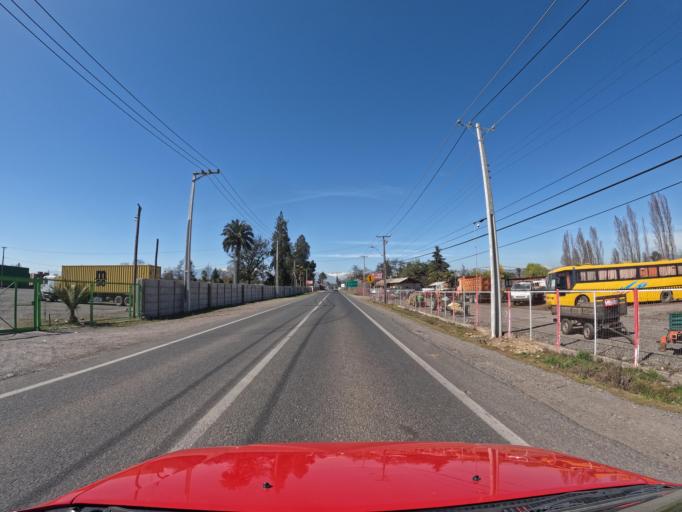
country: CL
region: Maule
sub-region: Provincia de Curico
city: Teno
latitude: -34.9611
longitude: -71.0978
